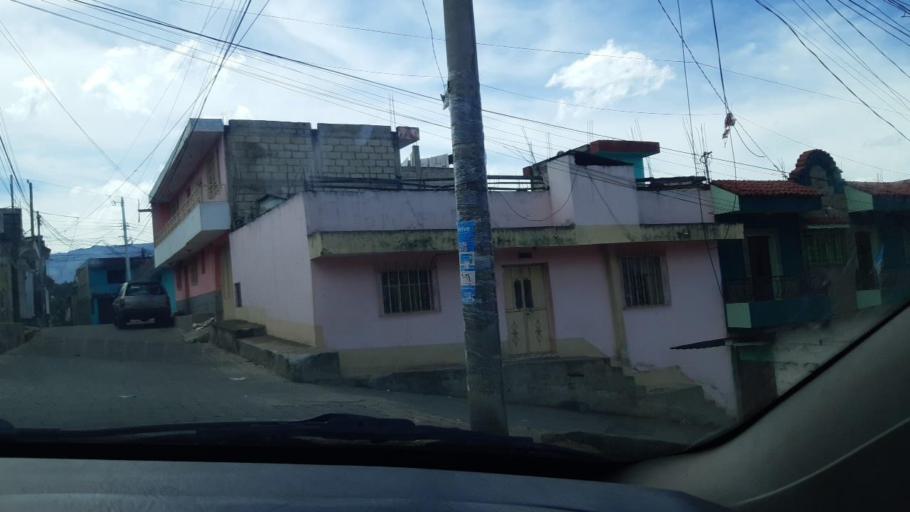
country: GT
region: Quetzaltenango
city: Salcaja
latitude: 14.8793
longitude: -91.4622
